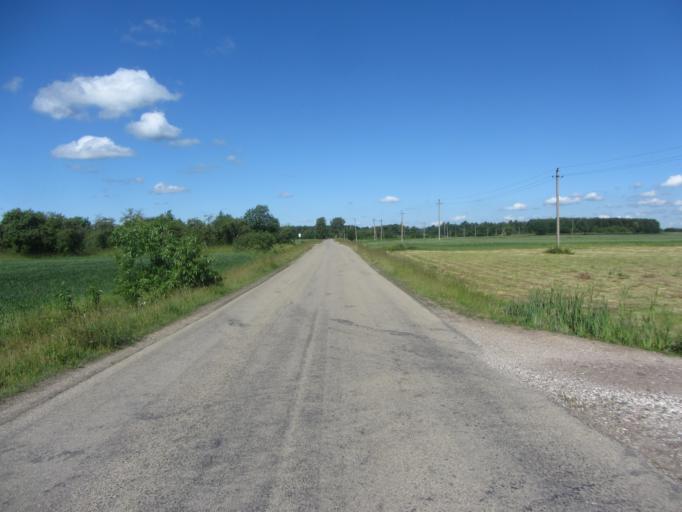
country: LT
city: Kaisiadorys
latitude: 54.8416
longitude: 24.2675
